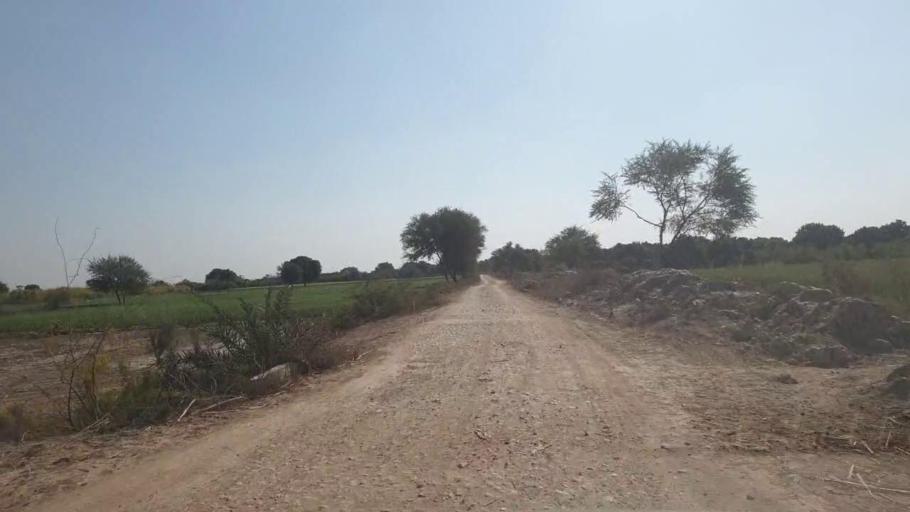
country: PK
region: Sindh
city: Chambar
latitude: 25.3141
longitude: 68.7409
